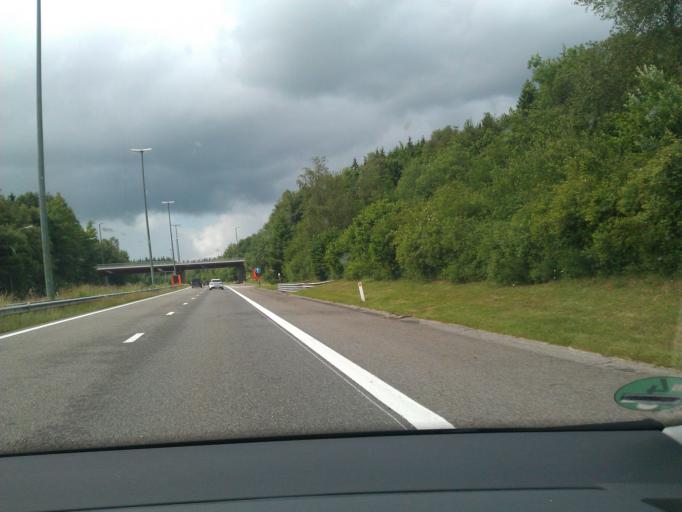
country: BE
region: Wallonia
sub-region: Province de Liege
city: Saint-Vith
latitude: 50.2530
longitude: 6.1700
